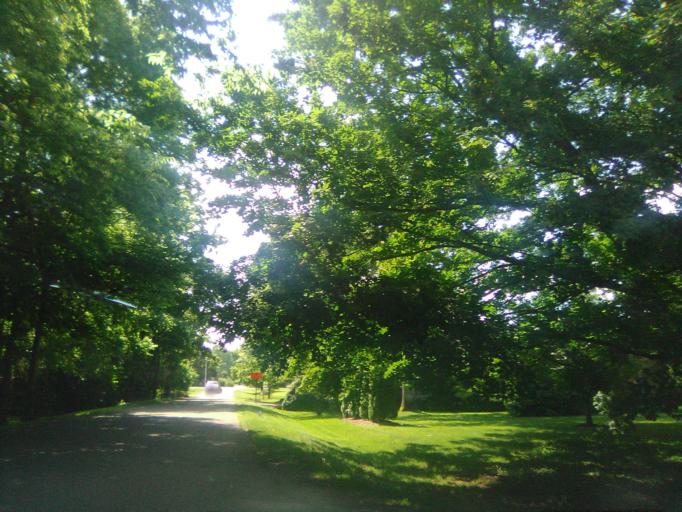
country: US
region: Tennessee
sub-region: Davidson County
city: Belle Meade
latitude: 36.1116
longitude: -86.8695
